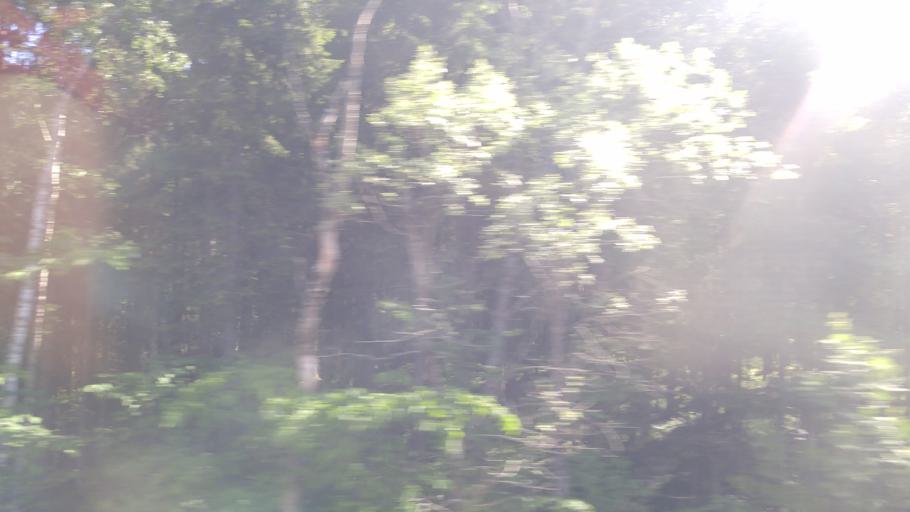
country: NO
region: Sor-Trondelag
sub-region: Midtre Gauldal
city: Storen
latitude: 62.9959
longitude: 10.4720
